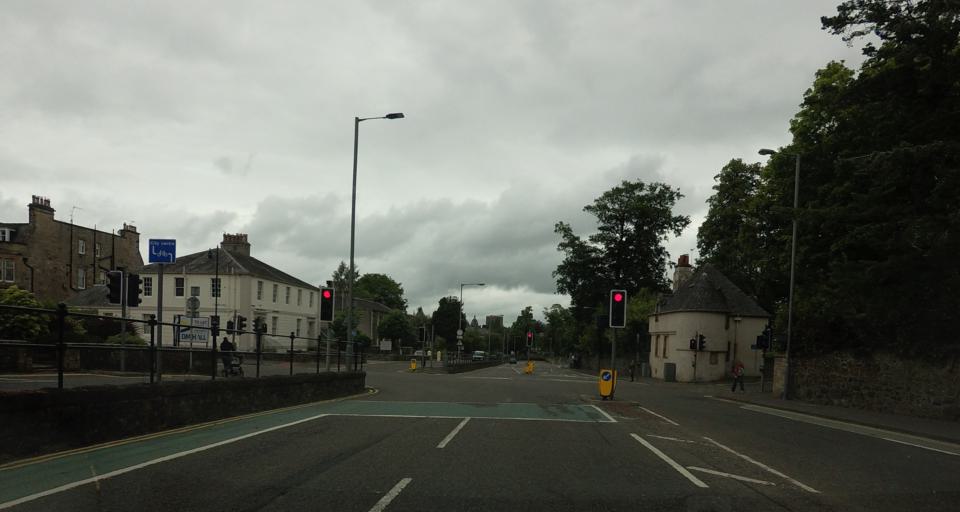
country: GB
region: Scotland
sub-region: Stirling
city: Stirling
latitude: 56.1115
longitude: -3.9386
